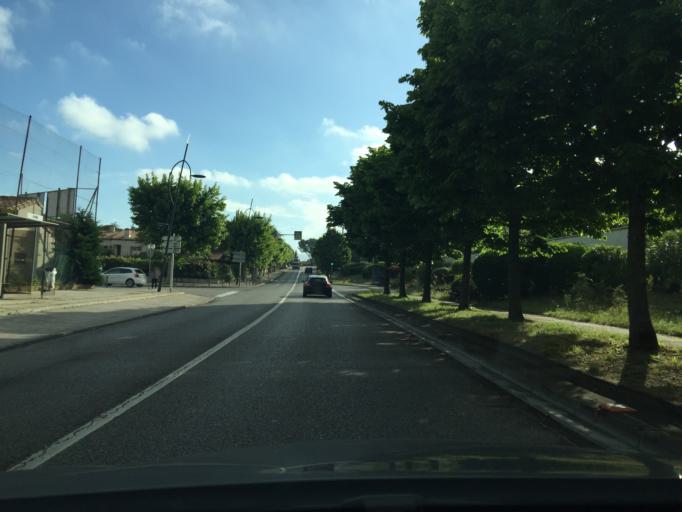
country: FR
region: Provence-Alpes-Cote d'Azur
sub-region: Departement des Bouches-du-Rhone
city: Carnoux-en-Provence
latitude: 43.2497
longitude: 5.5533
